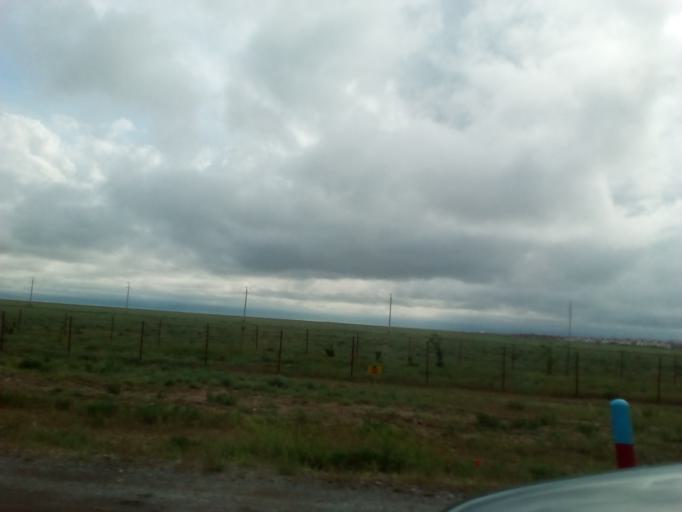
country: KZ
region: Ongtustik Qazaqstan
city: Sholaqqkorghan
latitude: 43.7470
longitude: 69.1989
